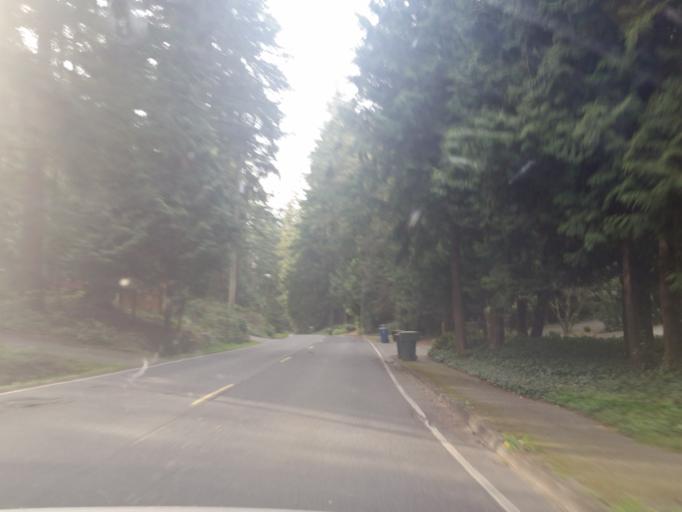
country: US
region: Washington
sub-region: Snohomish County
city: Meadowdale
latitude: 47.8417
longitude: -122.3264
